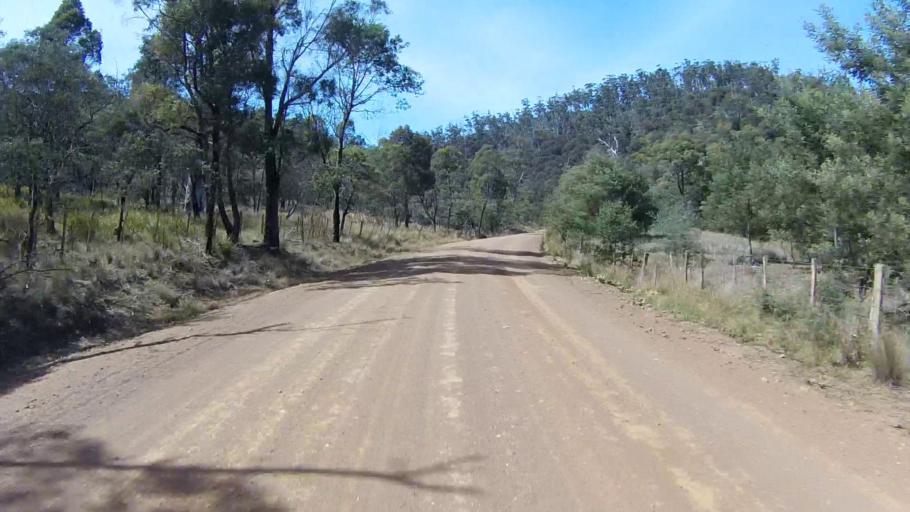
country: AU
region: Tasmania
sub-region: Sorell
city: Sorell
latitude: -42.6380
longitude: 147.7276
